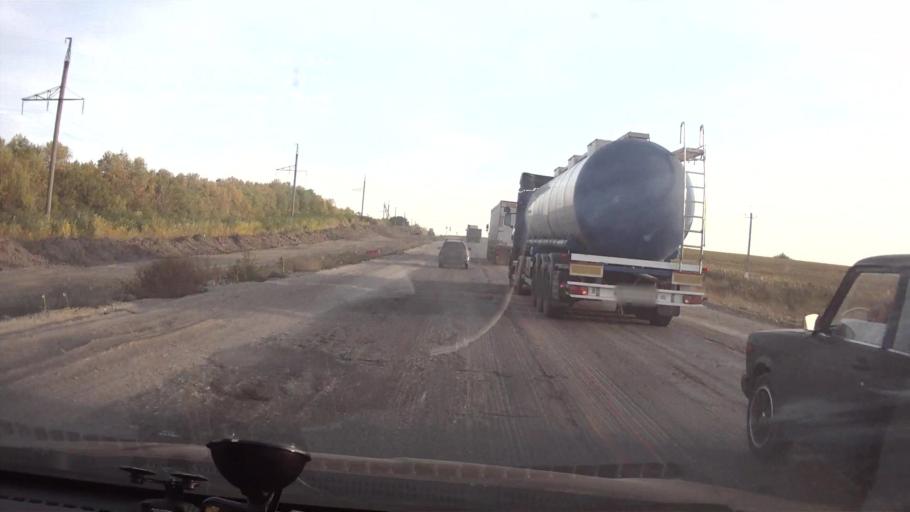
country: RU
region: Saratov
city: Krasnoarmeysk
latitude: 51.1919
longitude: 45.6481
